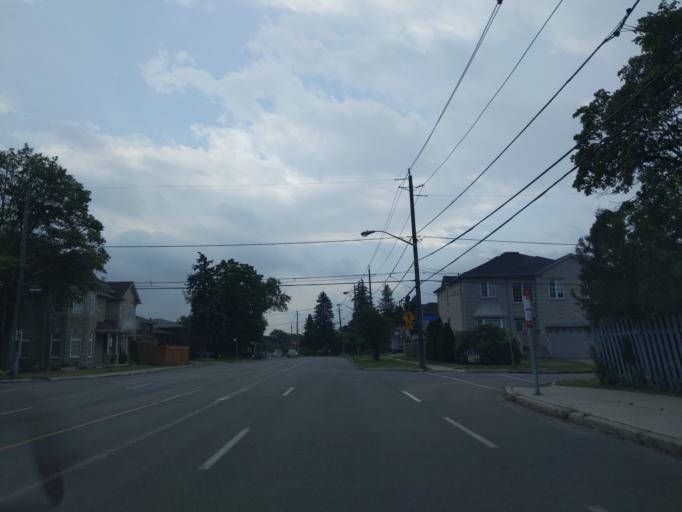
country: CA
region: Ontario
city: North York
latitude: 43.7904
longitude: -79.4110
